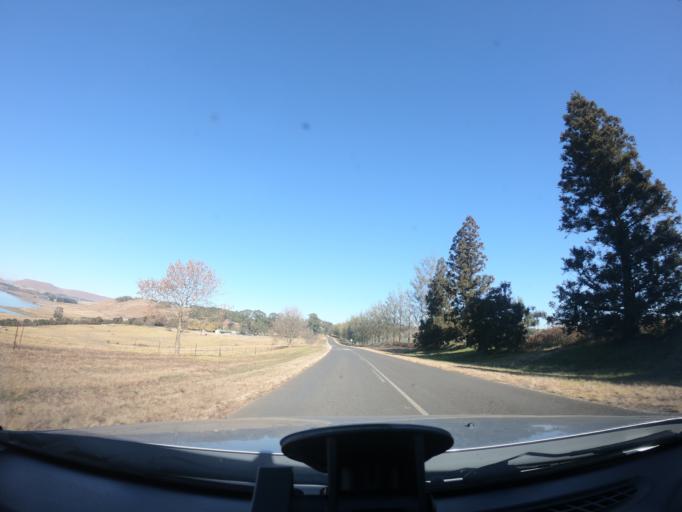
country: ZA
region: KwaZulu-Natal
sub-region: uMgungundlovu District Municipality
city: Mooirivier
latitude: -29.3145
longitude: 29.9252
